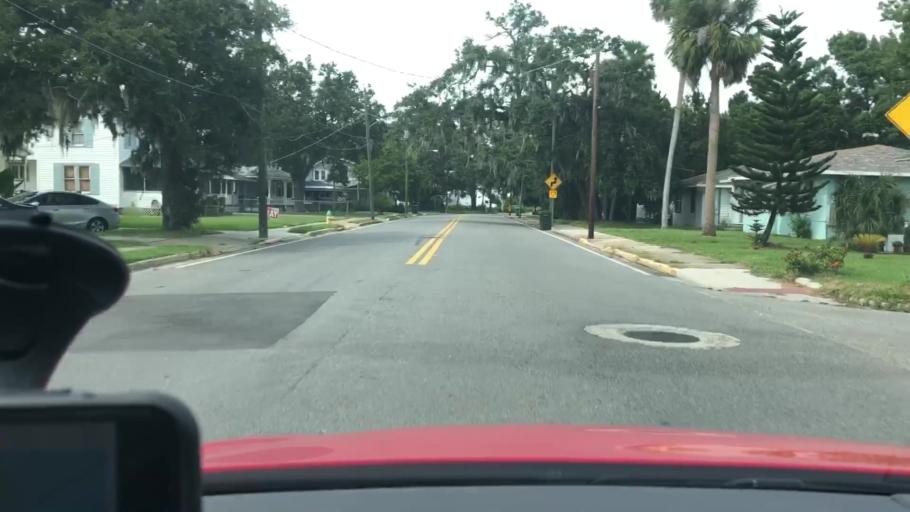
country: US
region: Florida
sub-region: Volusia County
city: Daytona Beach
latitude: 29.1970
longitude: -81.0127
